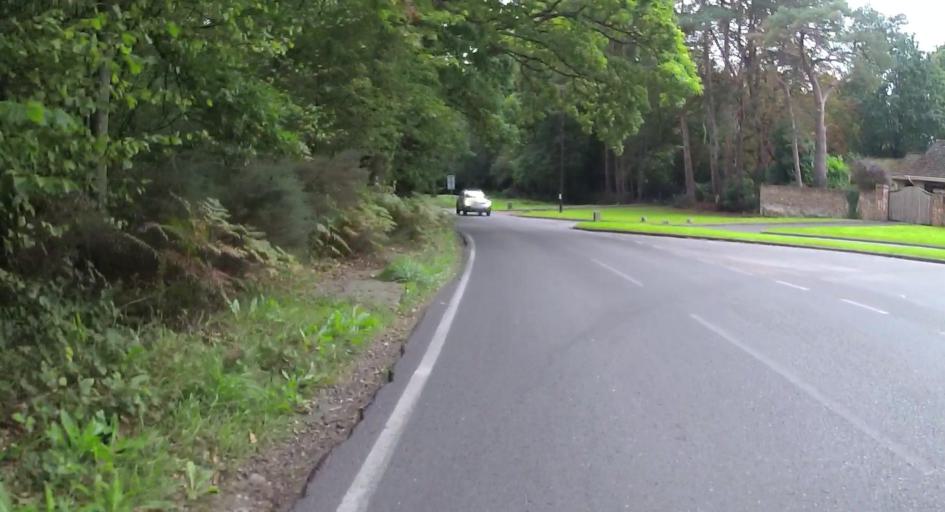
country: GB
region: England
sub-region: Surrey
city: Pirbright
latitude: 51.3082
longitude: -0.6526
